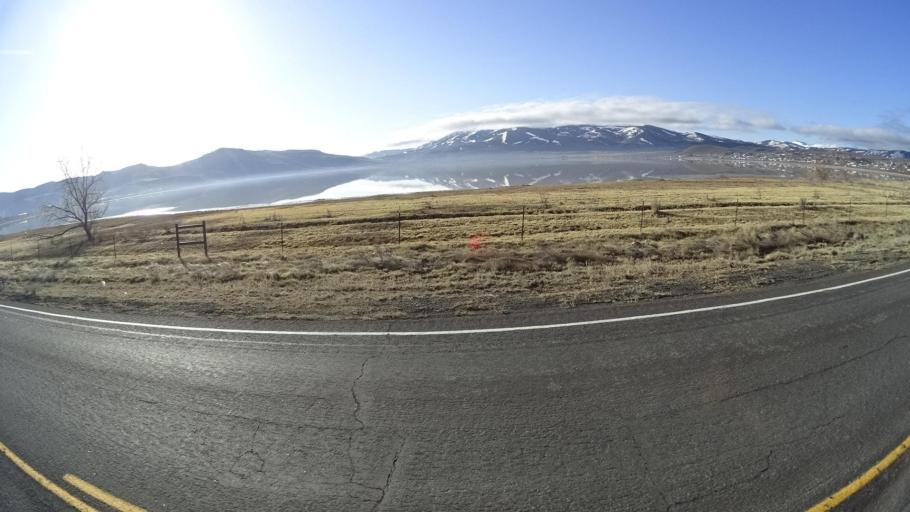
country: US
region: Nevada
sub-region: Washoe County
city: Cold Springs
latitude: 39.6727
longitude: -119.9859
